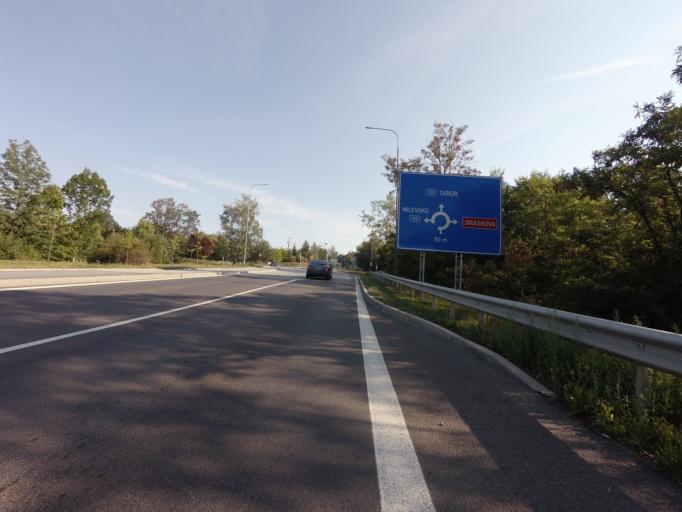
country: CZ
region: Jihocesky
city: Tyn nad Vltavou
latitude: 49.2274
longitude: 14.4244
